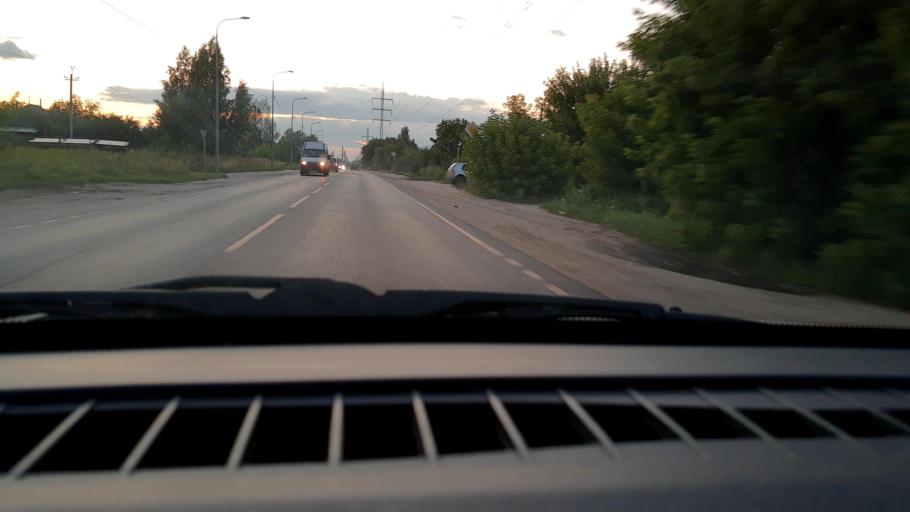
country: RU
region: Nizjnij Novgorod
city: Bor
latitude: 56.3714
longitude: 44.0654
